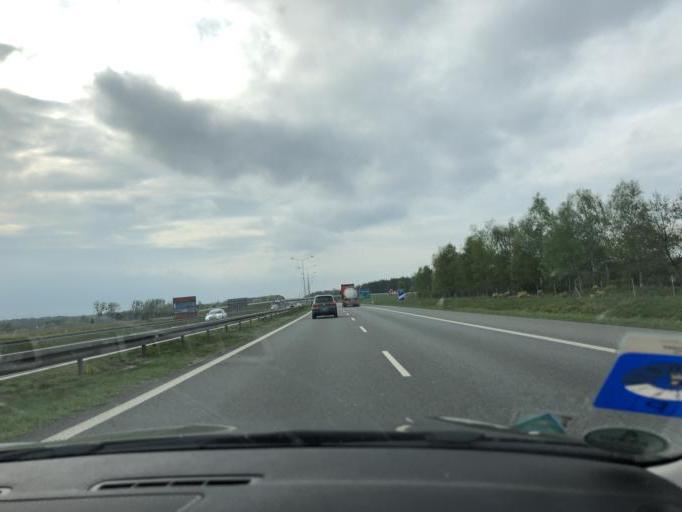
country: PL
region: Opole Voivodeship
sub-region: Powiat opolski
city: Dabrowa
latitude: 50.6584
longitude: 17.7075
